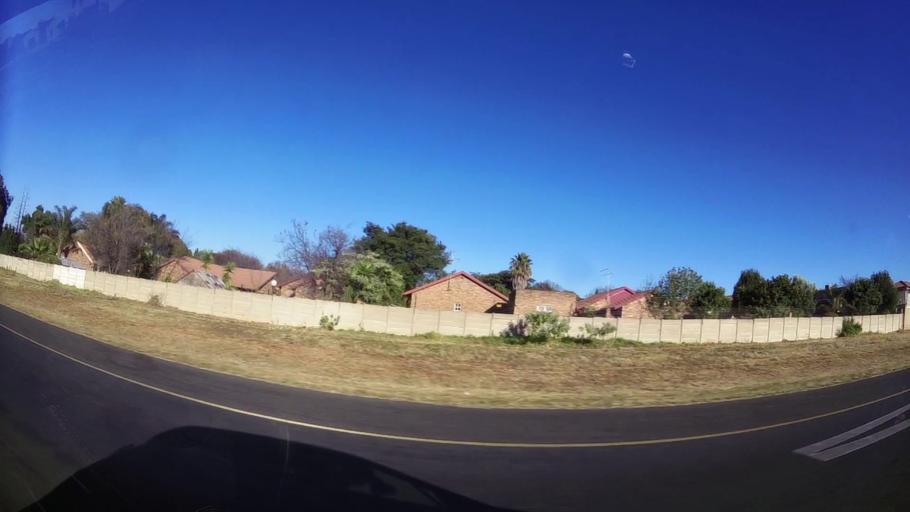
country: ZA
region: Gauteng
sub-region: City of Johannesburg Metropolitan Municipality
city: Modderfontein
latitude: -26.0797
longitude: 28.2039
